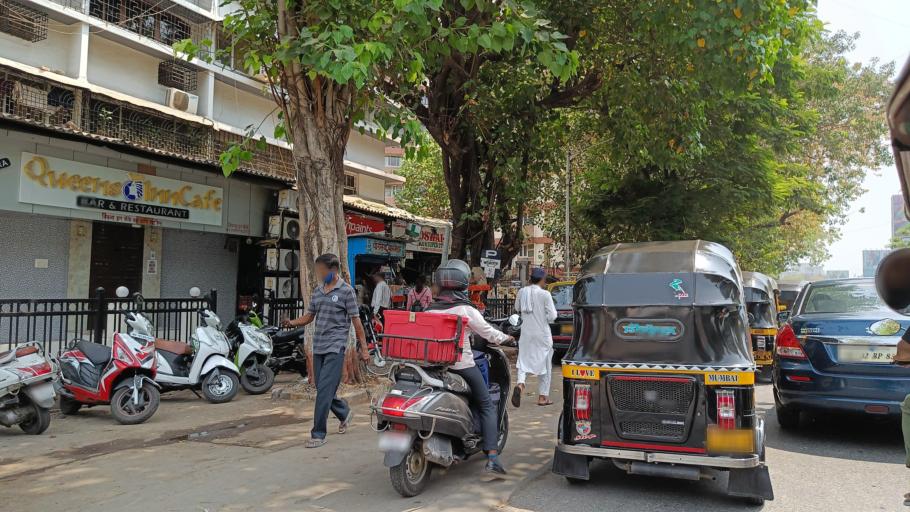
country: IN
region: Maharashtra
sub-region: Mumbai Suburban
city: Mumbai
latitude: 19.0859
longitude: 72.8286
